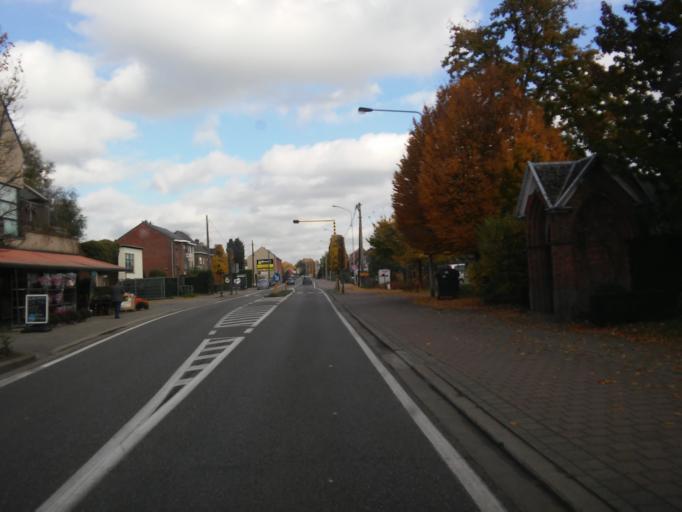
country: BE
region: Flanders
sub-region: Provincie Antwerpen
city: Duffel
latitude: 51.1006
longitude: 4.5094
